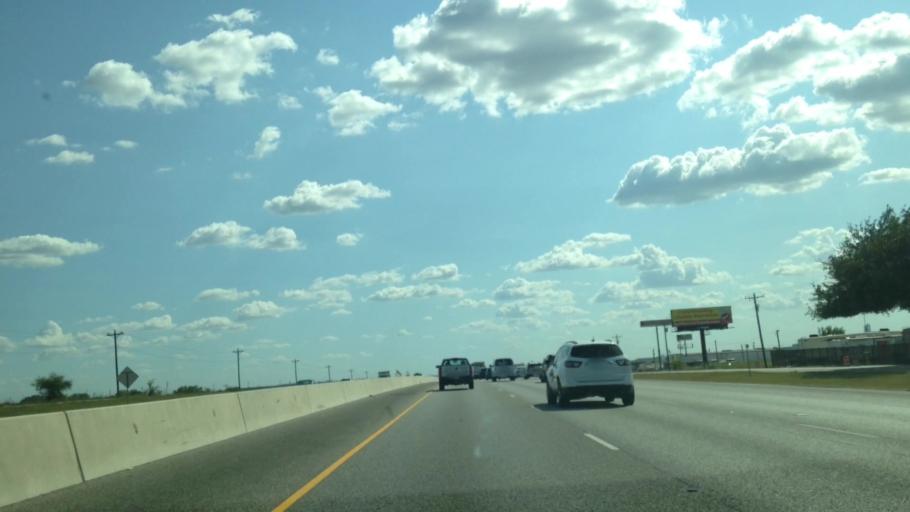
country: US
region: Texas
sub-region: Hays County
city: San Marcos
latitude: 29.8228
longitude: -97.9918
